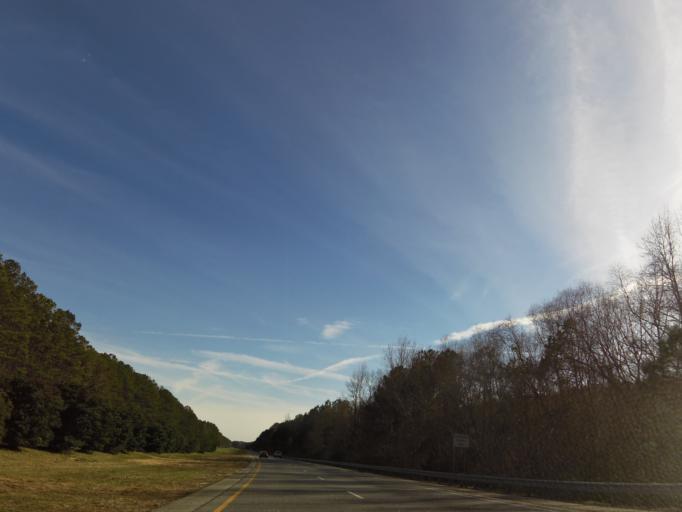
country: US
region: Georgia
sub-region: Harris County
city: Hamilton
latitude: 32.7182
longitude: -85.0184
